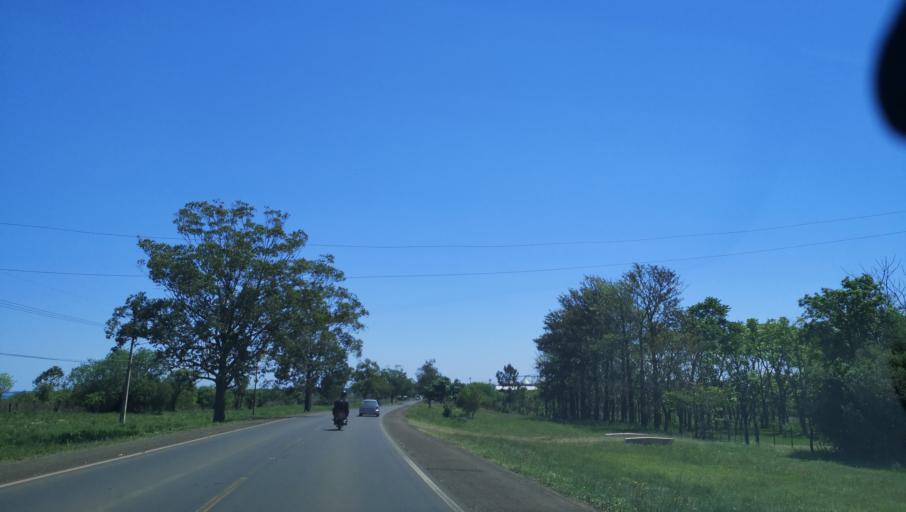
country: PY
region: Itapua
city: Carmen del Parana
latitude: -27.2216
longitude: -56.1186
